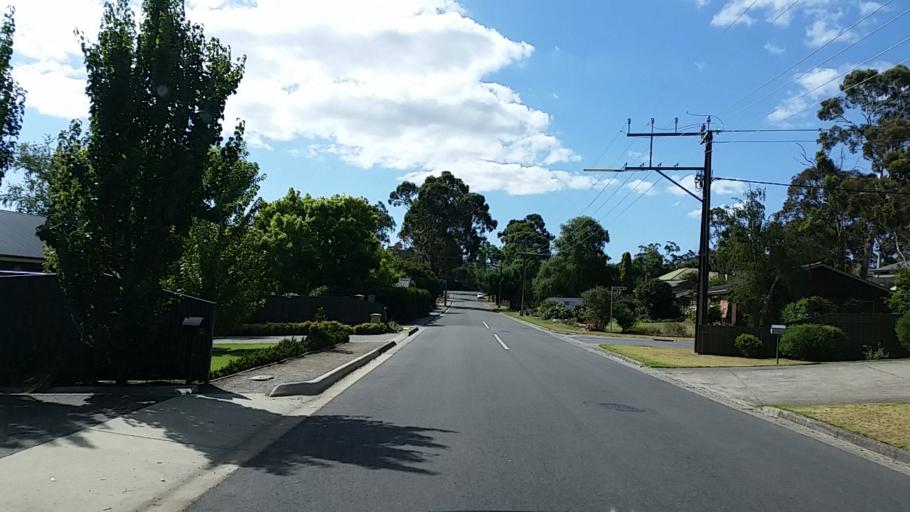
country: AU
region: South Australia
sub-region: Mount Barker
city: Hahndorf
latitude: -35.0283
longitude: 138.8162
